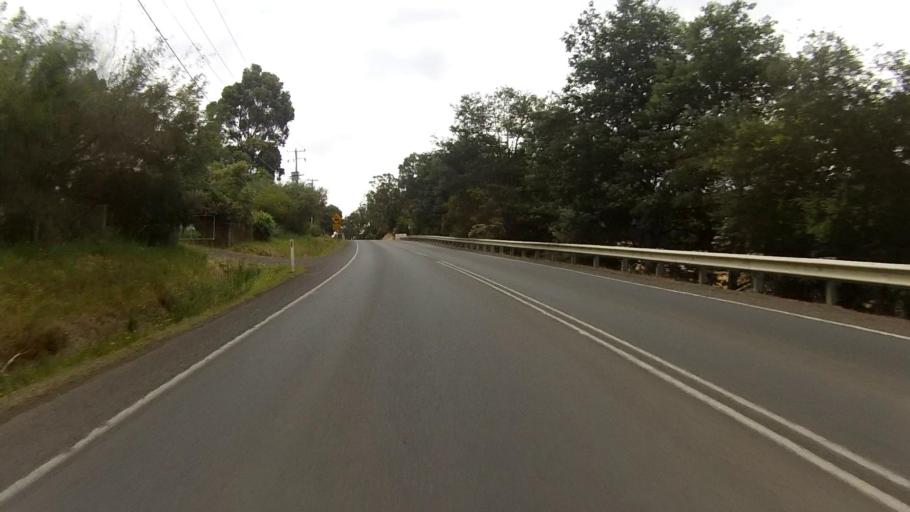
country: AU
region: Tasmania
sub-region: Huon Valley
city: Cygnet
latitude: -43.1290
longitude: 147.0474
